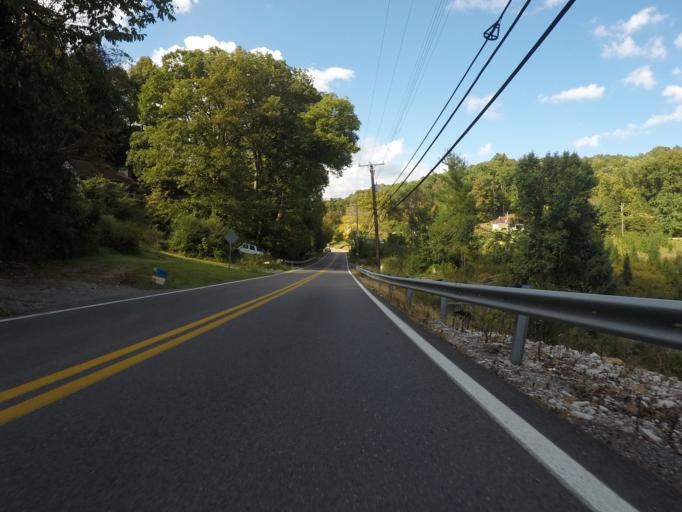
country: US
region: Ohio
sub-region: Lawrence County
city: Burlington
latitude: 38.3862
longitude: -82.5108
